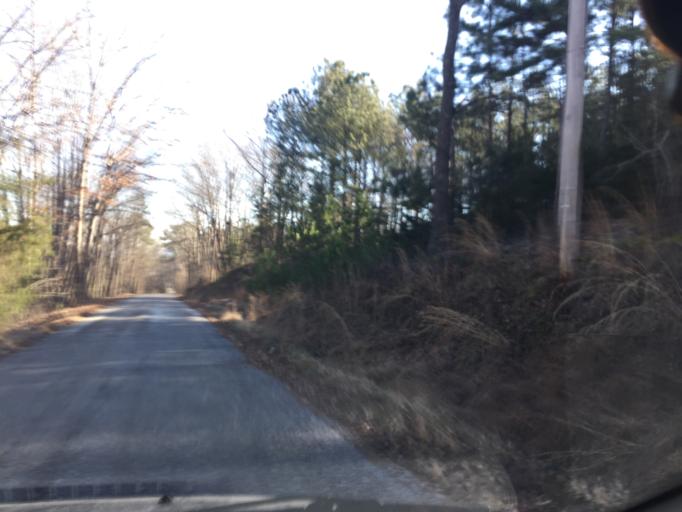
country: US
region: Tennessee
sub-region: Hamilton County
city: Collegedale
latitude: 35.0757
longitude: -85.0957
